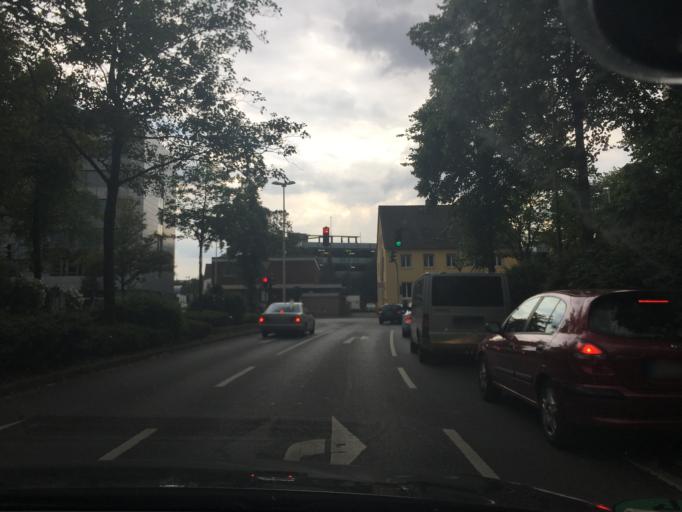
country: DE
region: North Rhine-Westphalia
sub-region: Regierungsbezirk Koln
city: Dueren
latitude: 50.8058
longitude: 6.4850
